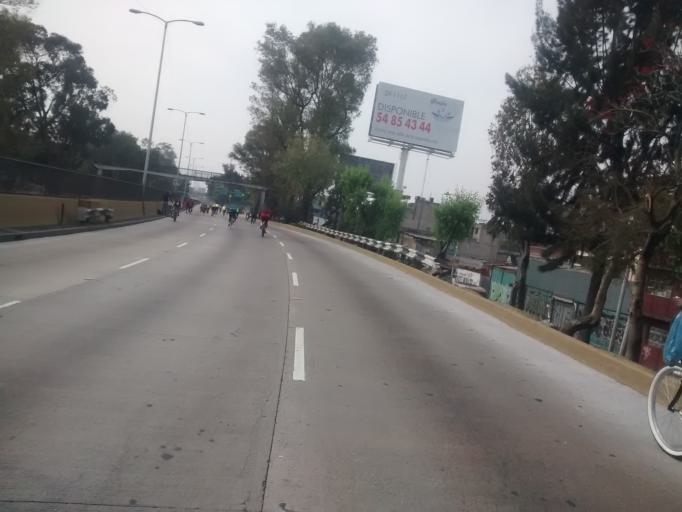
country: MX
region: Mexico City
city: Colonia Nativitas
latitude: 19.3684
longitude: -99.1254
